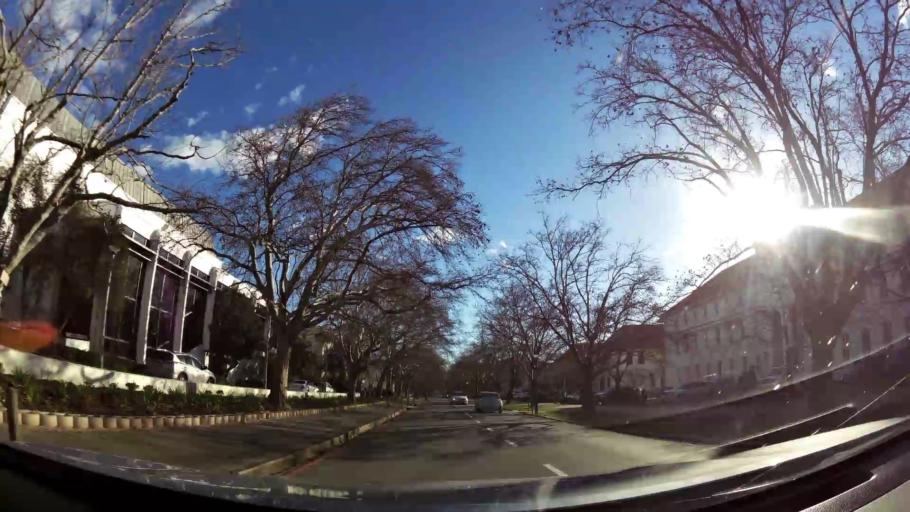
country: ZA
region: Western Cape
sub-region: Cape Winelands District Municipality
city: Stellenbosch
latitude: -33.9338
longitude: 18.8667
